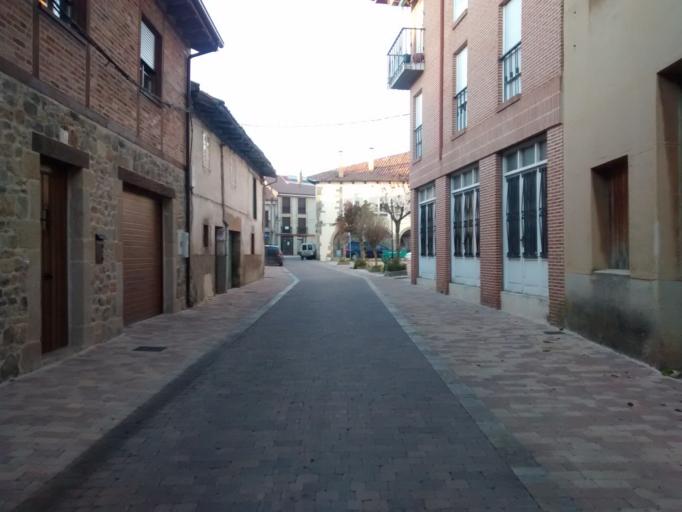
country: ES
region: Castille and Leon
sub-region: Provincia de Palencia
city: Aguilar de Campoo
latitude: 42.7925
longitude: -4.2575
